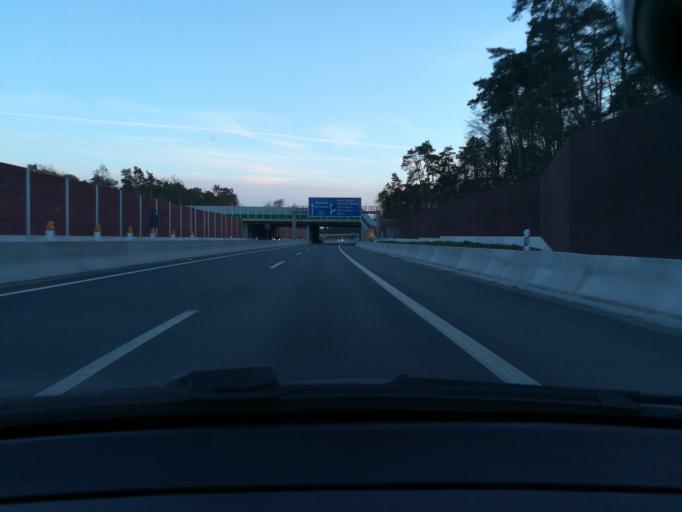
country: DE
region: North Rhine-Westphalia
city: Halle
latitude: 52.0502
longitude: 8.3403
